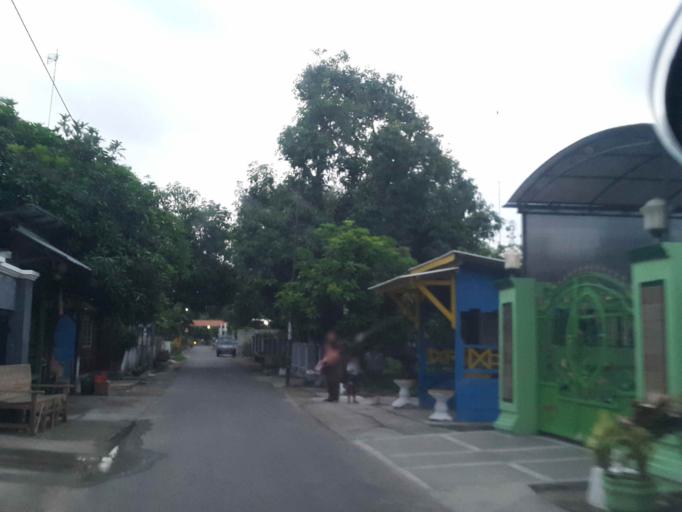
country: ID
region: Central Java
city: Kasingan
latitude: -6.7063
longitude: 111.3542
